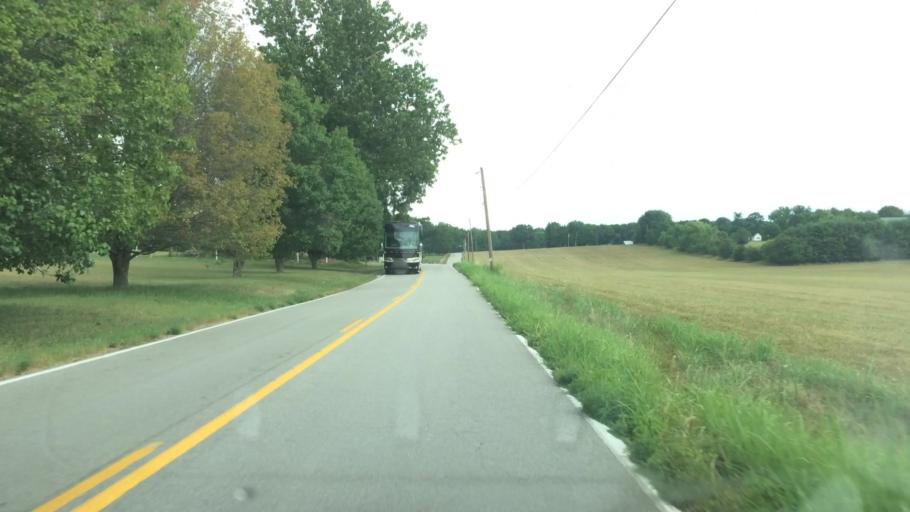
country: US
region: Missouri
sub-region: Greene County
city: Strafford
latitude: 37.1849
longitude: -93.1847
